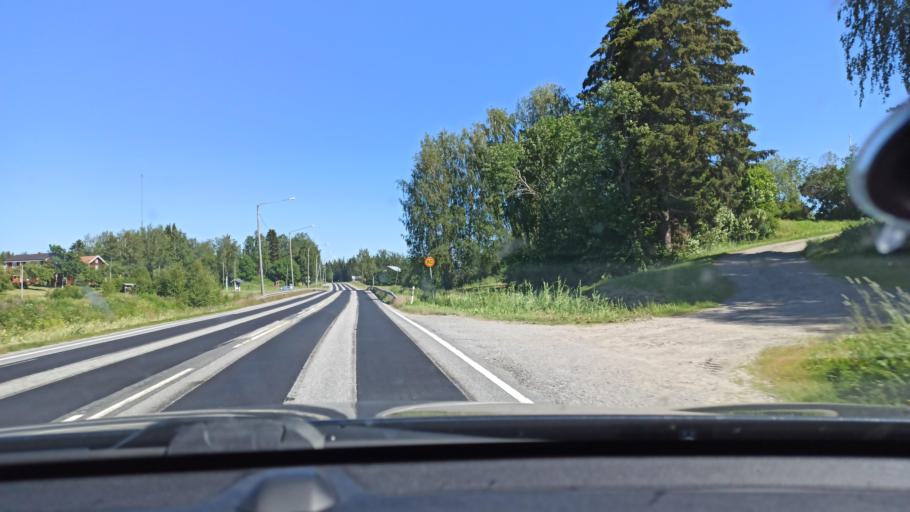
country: FI
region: Ostrobothnia
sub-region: Vaasa
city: Vaehaekyroe
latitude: 63.2024
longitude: 22.1059
